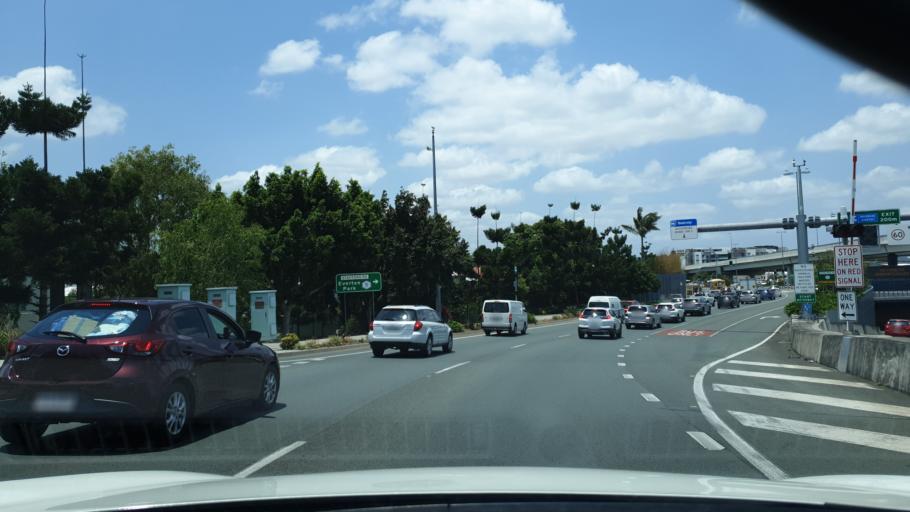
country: AU
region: Queensland
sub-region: Brisbane
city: Gordon Park
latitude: -27.4109
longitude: 153.0337
